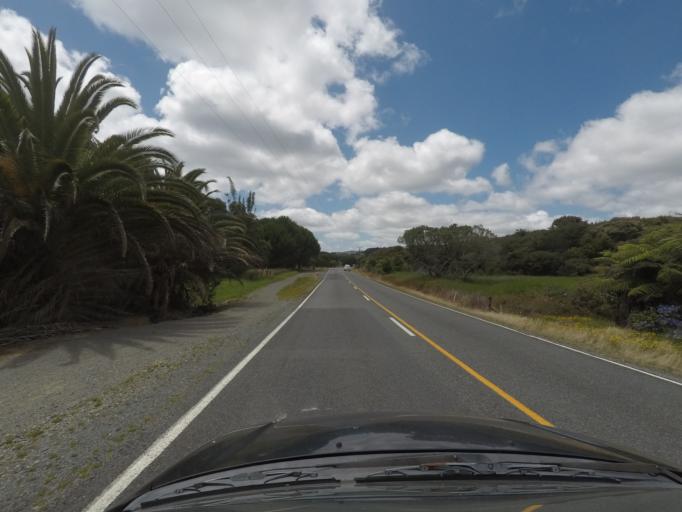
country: NZ
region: Northland
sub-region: Whangarei
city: Ruakaka
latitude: -36.0236
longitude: 174.4985
